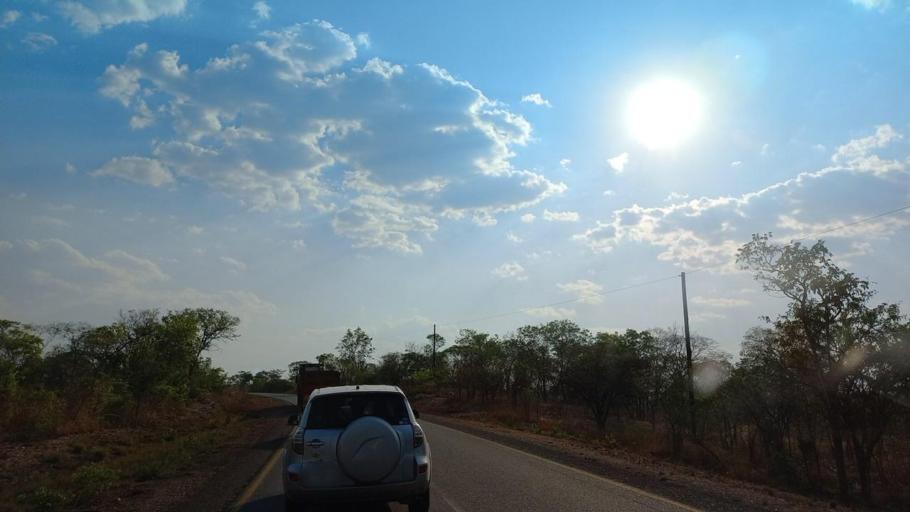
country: ZM
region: Lusaka
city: Luangwa
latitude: -14.9792
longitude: 29.9919
